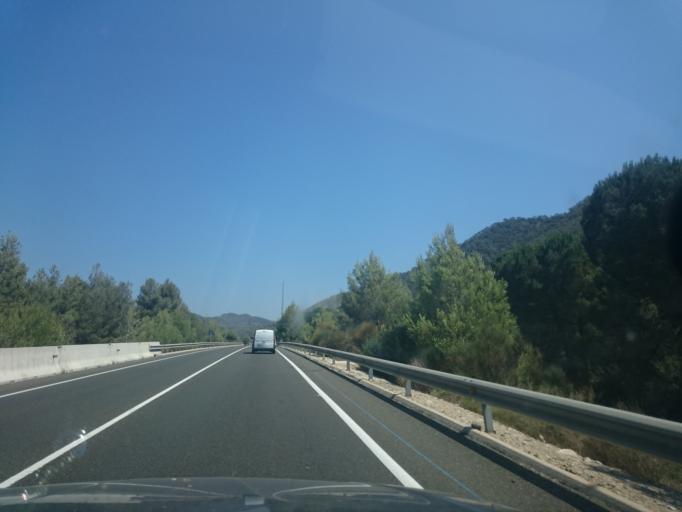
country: ES
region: Catalonia
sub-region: Provincia de Barcelona
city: Capellades
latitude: 41.5375
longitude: 1.6909
